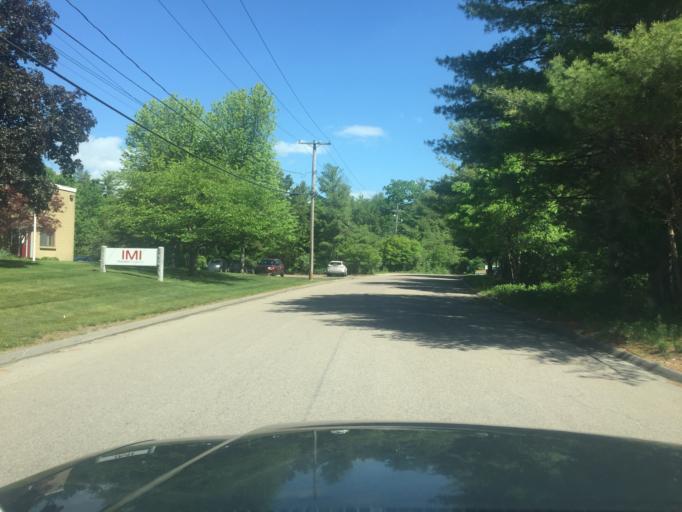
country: US
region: Massachusetts
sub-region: Norfolk County
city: Medway
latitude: 42.1584
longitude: -71.3927
